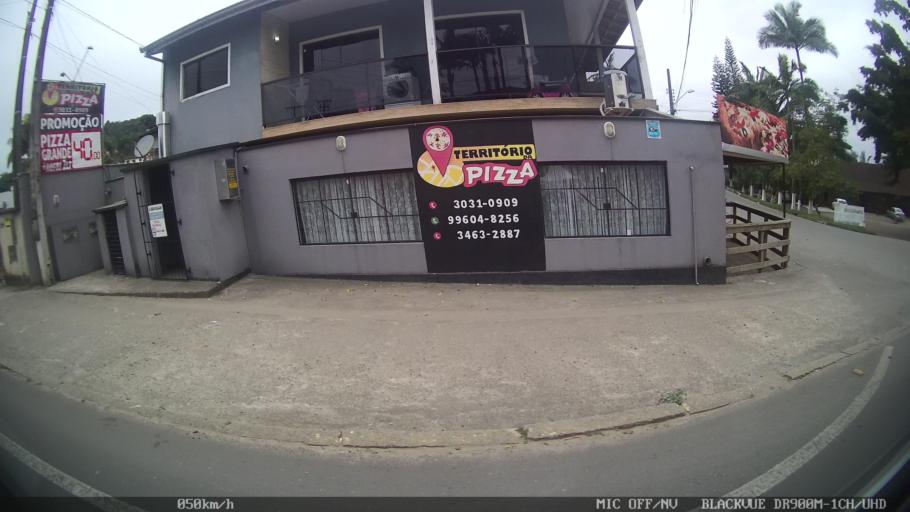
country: BR
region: Santa Catarina
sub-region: Joinville
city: Joinville
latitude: -26.3314
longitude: -48.8287
